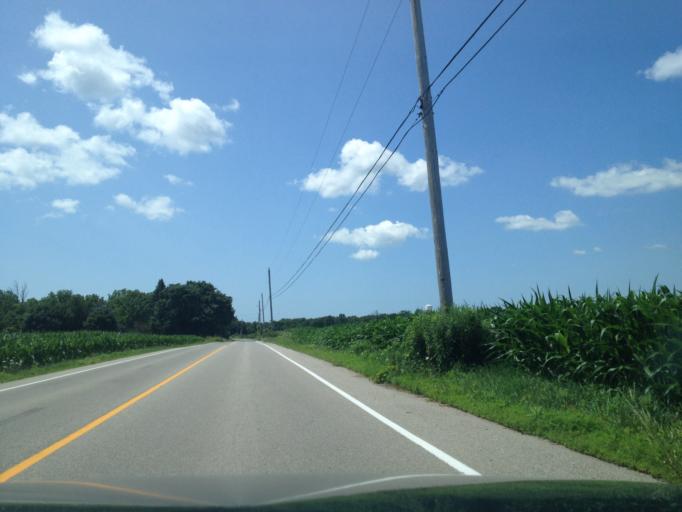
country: CA
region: Ontario
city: Norfolk County
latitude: 42.6376
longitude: -80.4385
